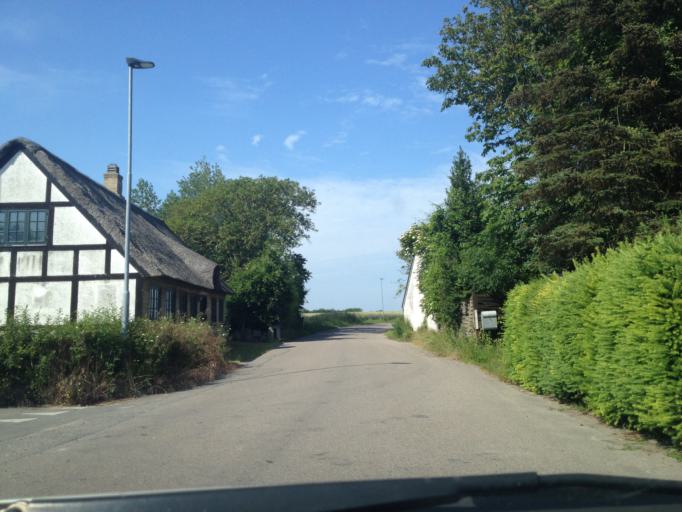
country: DK
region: Central Jutland
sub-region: Samso Kommune
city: Tranebjerg
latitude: 55.8398
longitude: 10.5560
